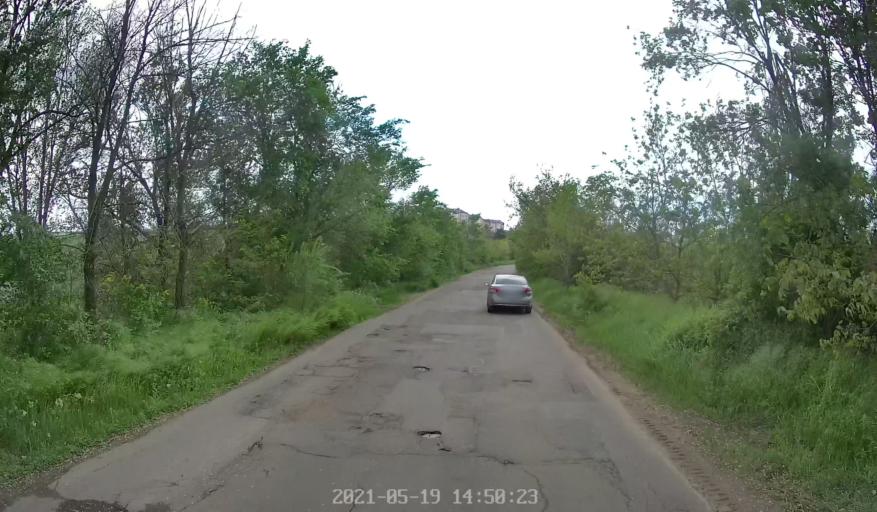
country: MD
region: Chisinau
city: Stauceni
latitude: 47.0559
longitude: 28.9464
